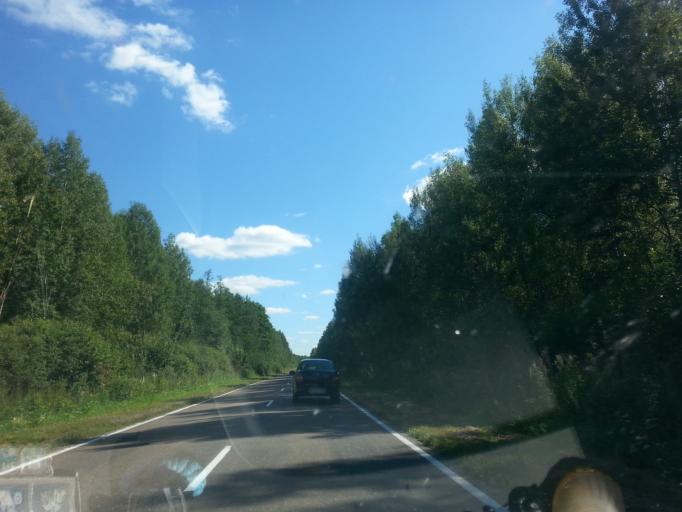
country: RU
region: Vladimir
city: Galitsy
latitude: 56.1448
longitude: 42.8653
